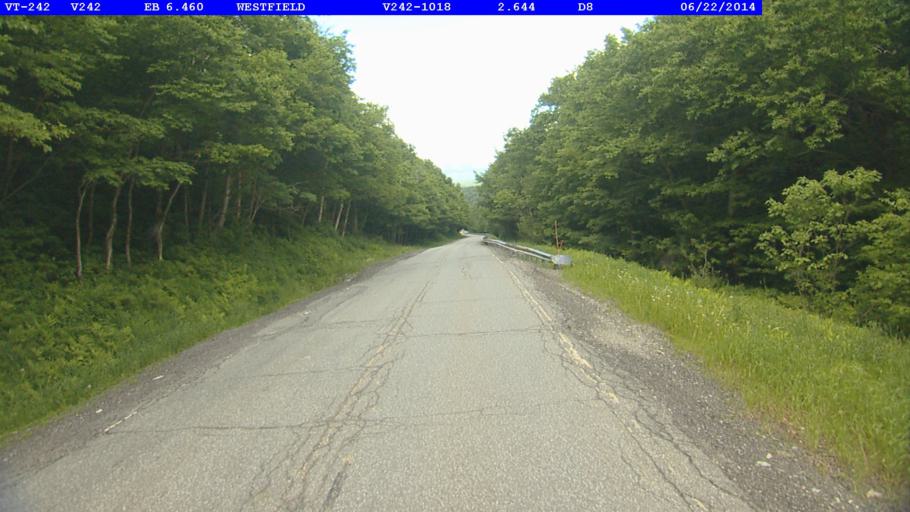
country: US
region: Vermont
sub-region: Franklin County
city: Richford
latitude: 44.9143
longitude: -72.5028
